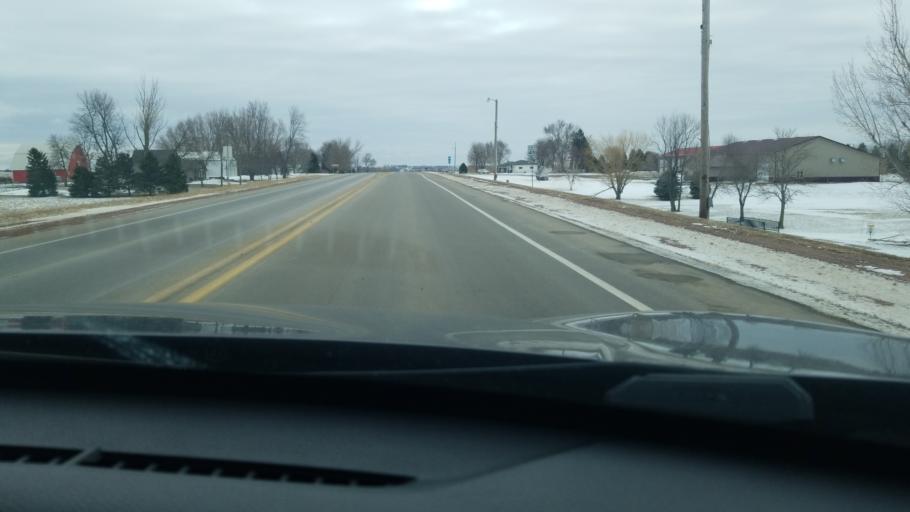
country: US
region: South Dakota
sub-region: Minnehaha County
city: Brandon
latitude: 43.4505
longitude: -96.4297
